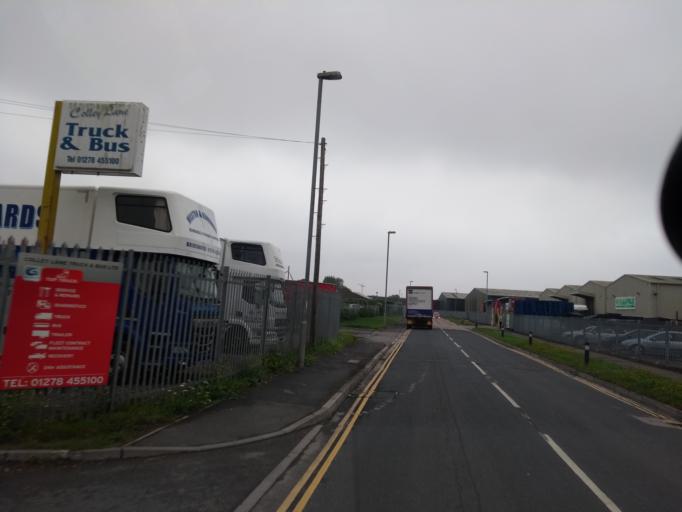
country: GB
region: England
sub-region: Somerset
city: Bridgwater
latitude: 51.1210
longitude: -2.9927
